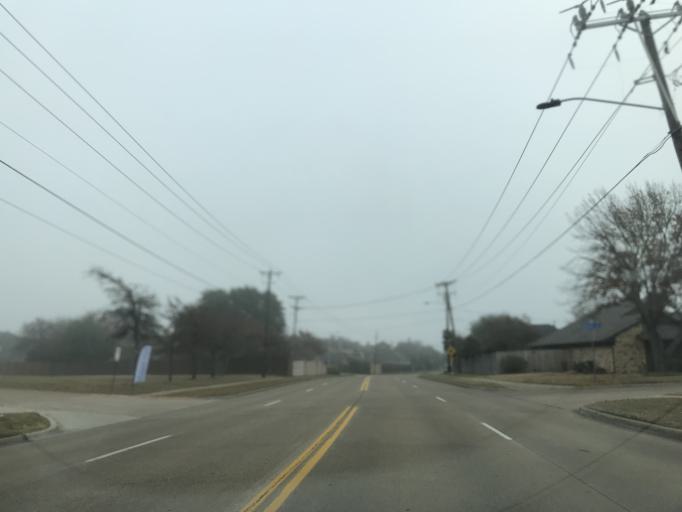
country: US
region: Texas
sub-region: Tarrant County
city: Arlington
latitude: 32.7744
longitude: -97.0771
